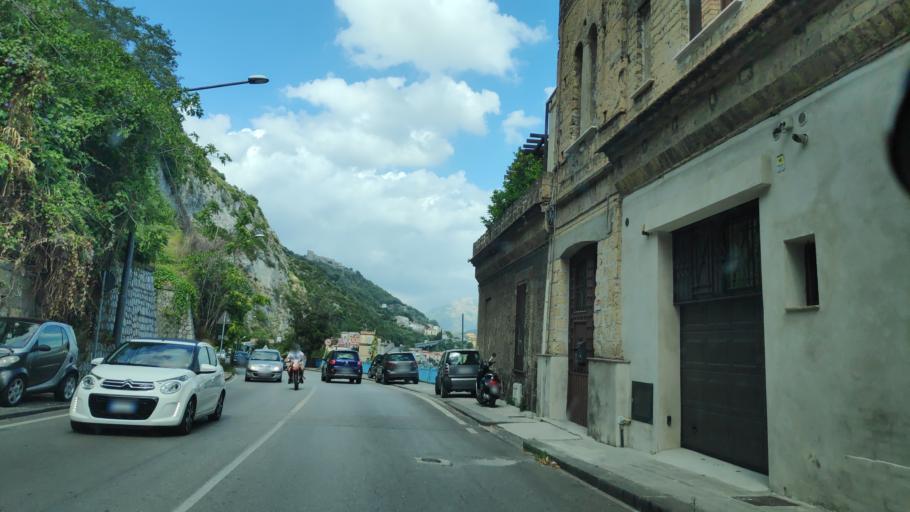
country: IT
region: Campania
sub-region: Provincia di Salerno
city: Vietri sul Mare
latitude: 40.6758
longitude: 14.7374
